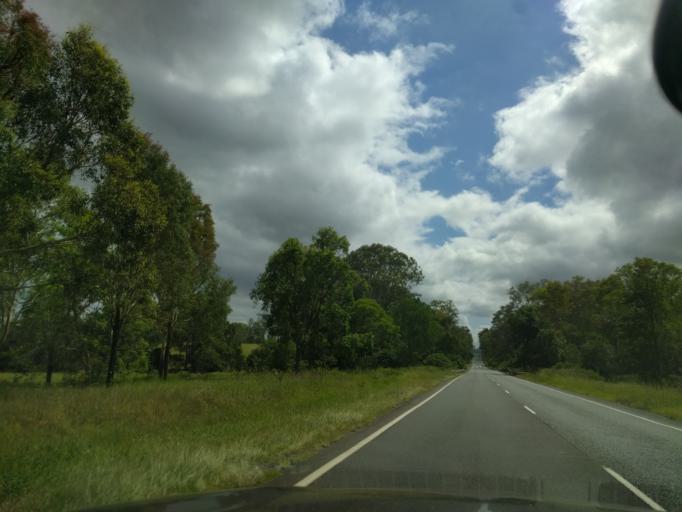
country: AU
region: Queensland
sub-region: Logan
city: Cedar Vale
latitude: -27.8579
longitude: 153.0051
